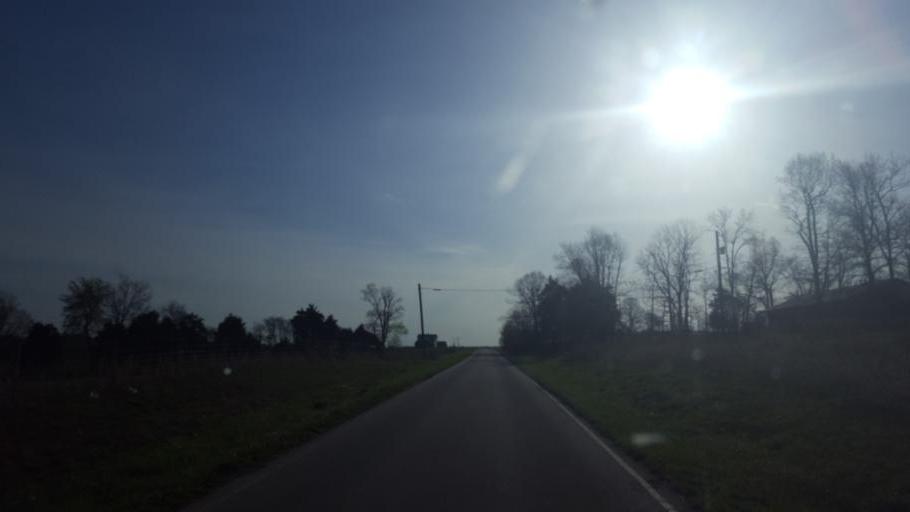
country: US
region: Kentucky
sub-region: Hart County
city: Munfordville
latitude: 37.4847
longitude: -85.9521
